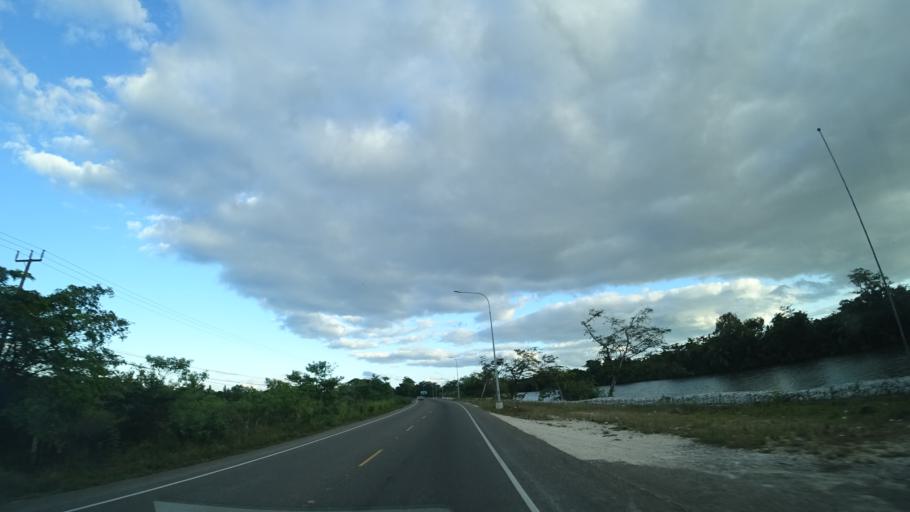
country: BZ
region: Belize
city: Belize City
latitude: 17.5459
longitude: -88.2753
